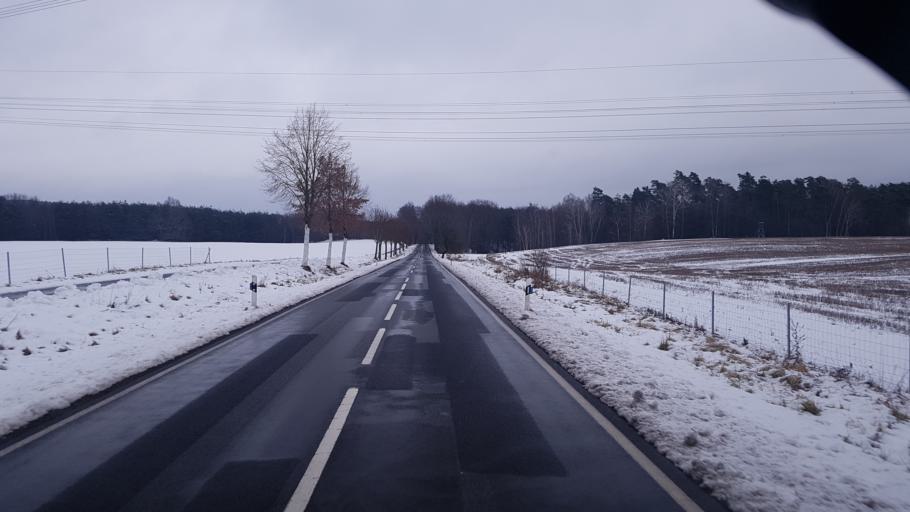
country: DE
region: Brandenburg
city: Lawitz
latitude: 52.0999
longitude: 14.5660
